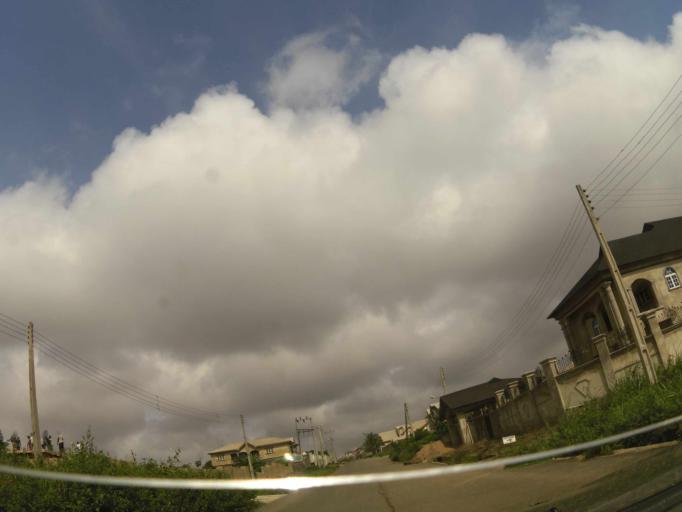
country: NG
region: Oyo
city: Ibadan
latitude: 7.4361
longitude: 3.9595
